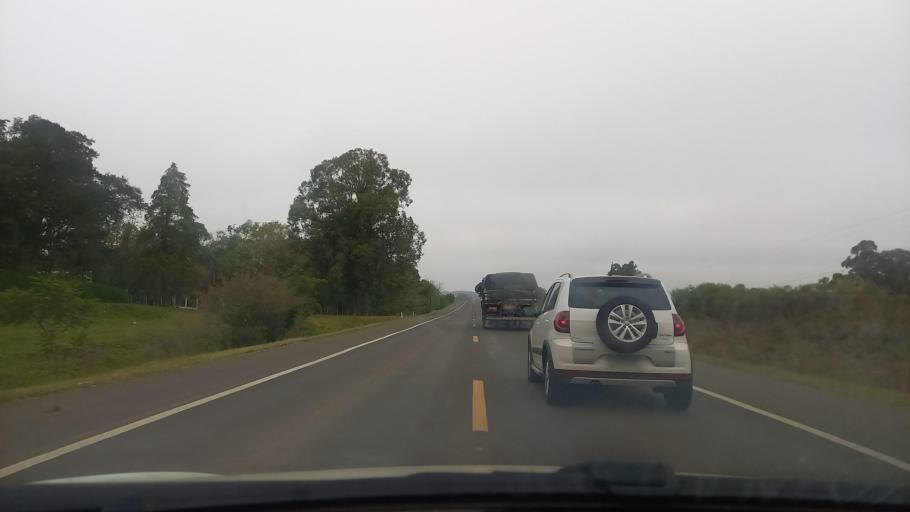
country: BR
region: Rio Grande do Sul
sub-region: Rosario Do Sul
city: Rosario do Sul
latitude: -30.2738
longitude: -54.9776
